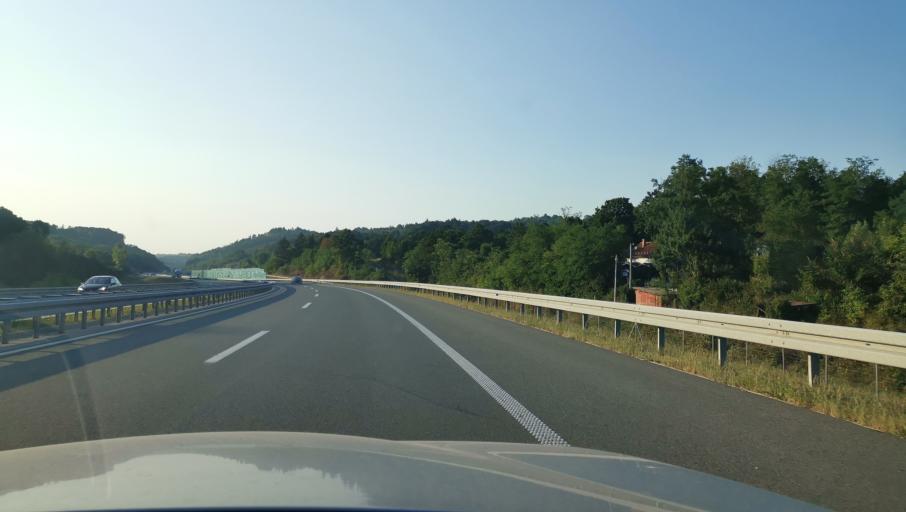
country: RS
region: Central Serbia
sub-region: Moravicki Okrug
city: Gornji Milanovac
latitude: 44.1252
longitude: 20.3670
